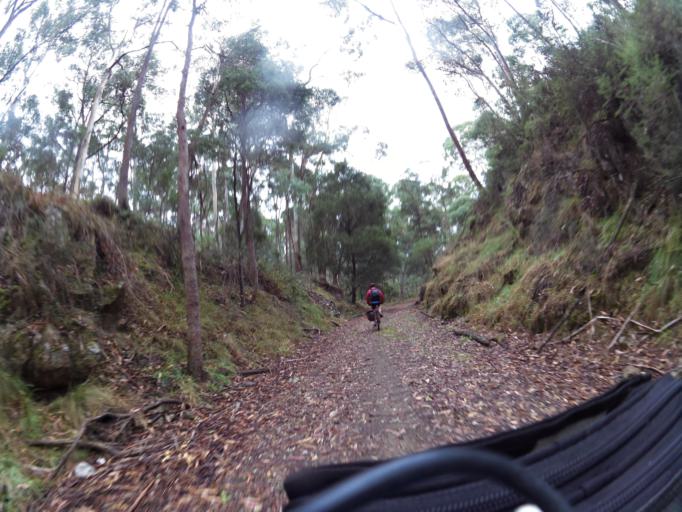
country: AU
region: New South Wales
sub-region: Greater Hume Shire
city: Holbrook
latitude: -36.1666
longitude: 147.4849
